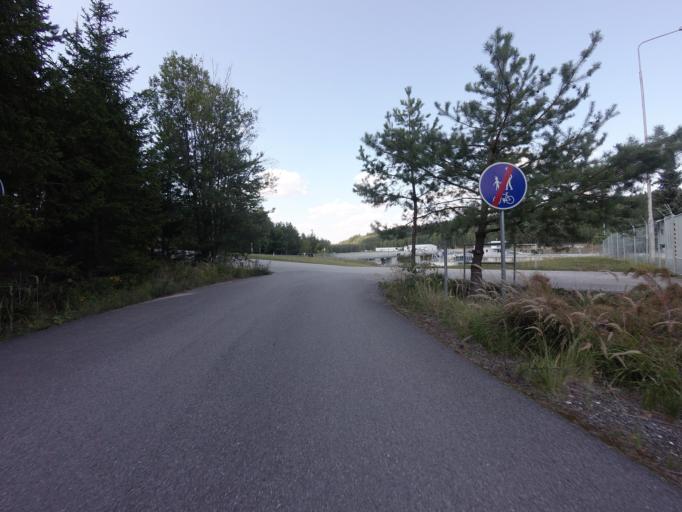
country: CZ
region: Jihocesky
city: Tyn nad Vltavou
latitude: 49.1804
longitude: 14.4448
